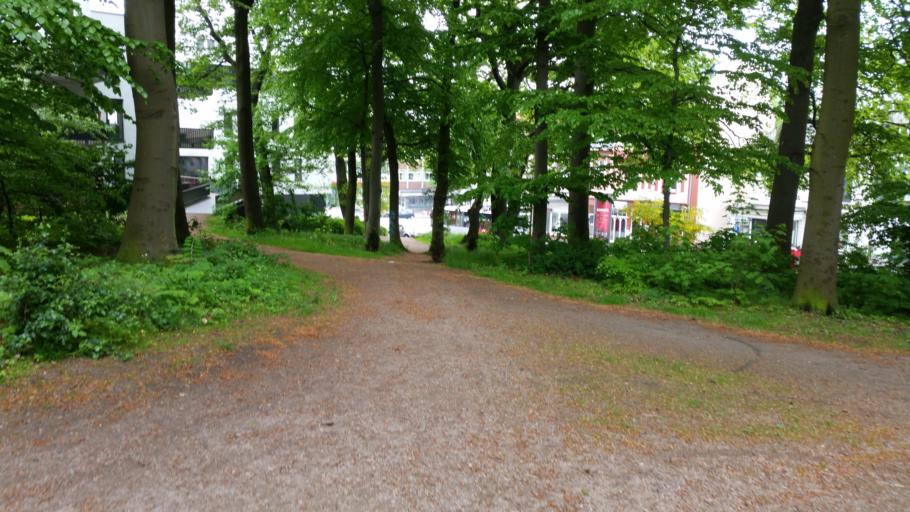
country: DE
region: Schleswig-Holstein
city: Halstenbek
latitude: 53.5636
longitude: 9.8110
